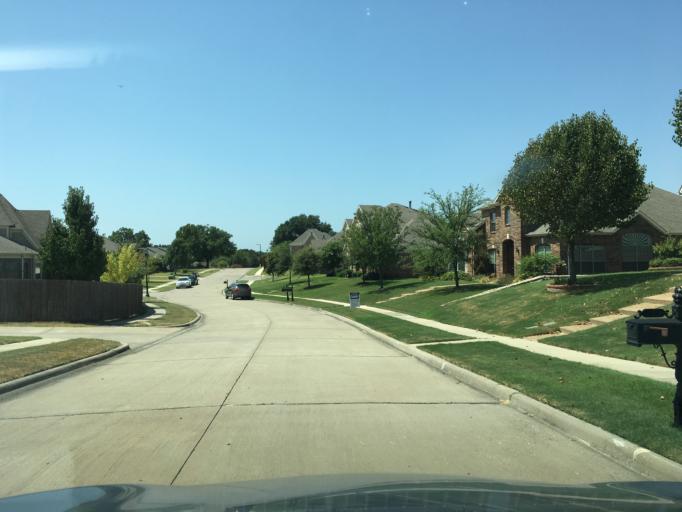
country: US
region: Texas
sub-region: Dallas County
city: Rowlett
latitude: 32.8871
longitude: -96.6009
